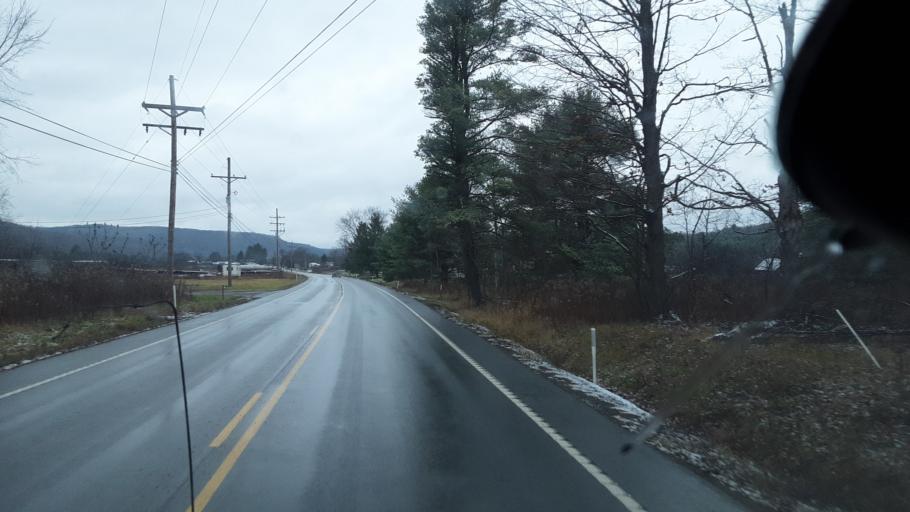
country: US
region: Pennsylvania
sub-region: Potter County
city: Shinglehouse
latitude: 41.9375
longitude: -78.1357
